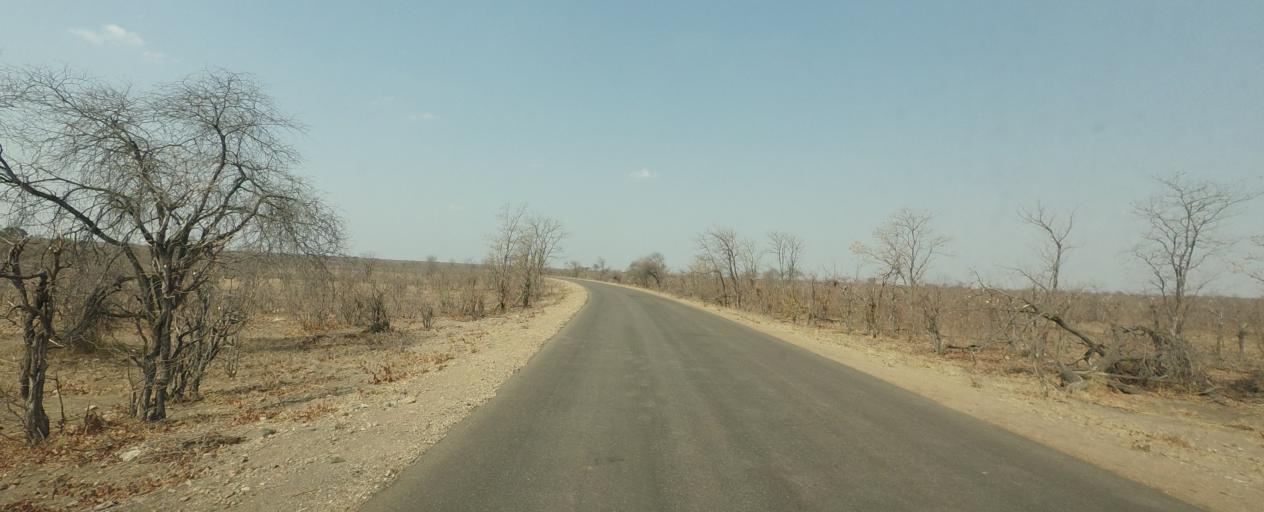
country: ZA
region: Limpopo
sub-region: Mopani District Municipality
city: Giyani
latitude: -23.1670
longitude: 31.3439
